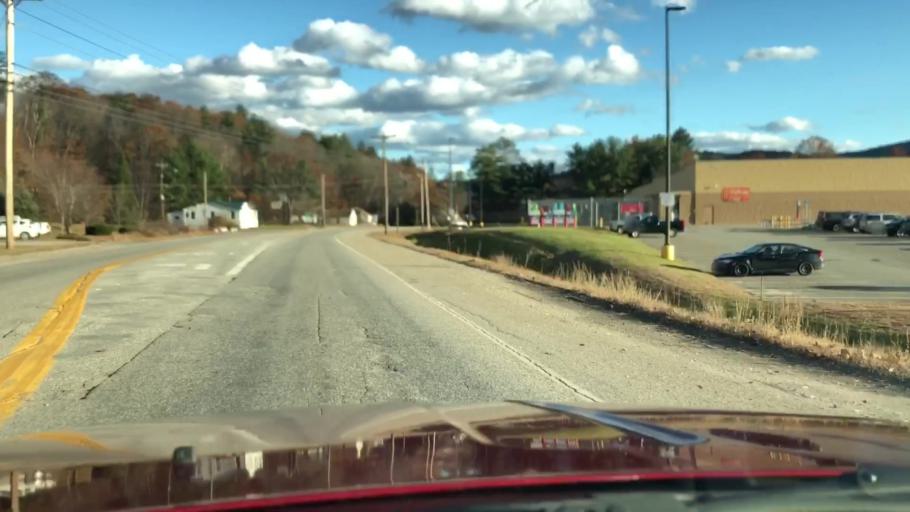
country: US
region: Maine
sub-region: Oxford County
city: Mexico
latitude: 44.5399
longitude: -70.5175
